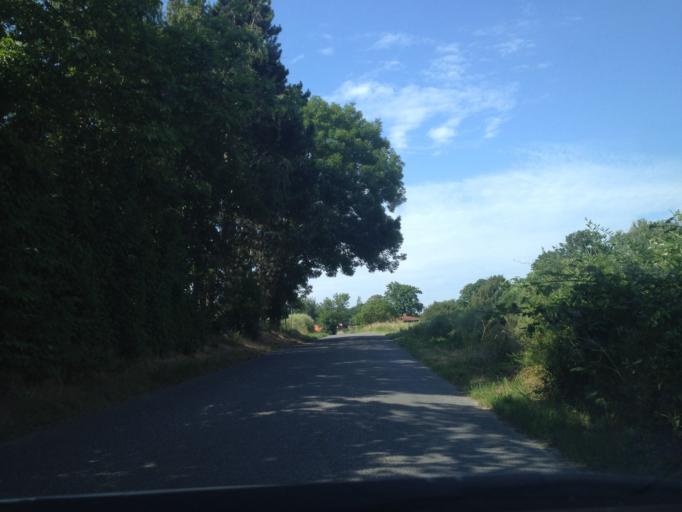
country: DK
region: Central Jutland
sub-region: Samso Kommune
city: Tranebjerg
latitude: 55.8139
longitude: 10.5548
